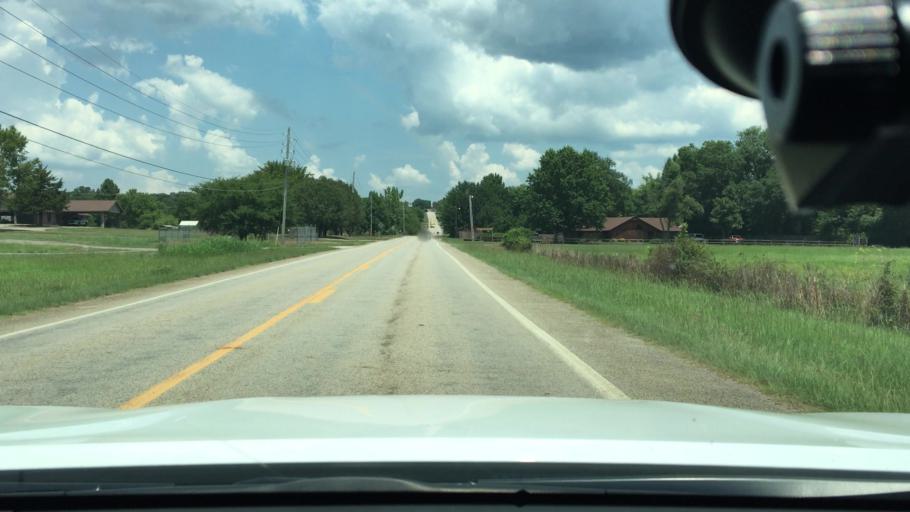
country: US
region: Arkansas
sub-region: Logan County
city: Booneville
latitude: 35.1486
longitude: -93.8772
